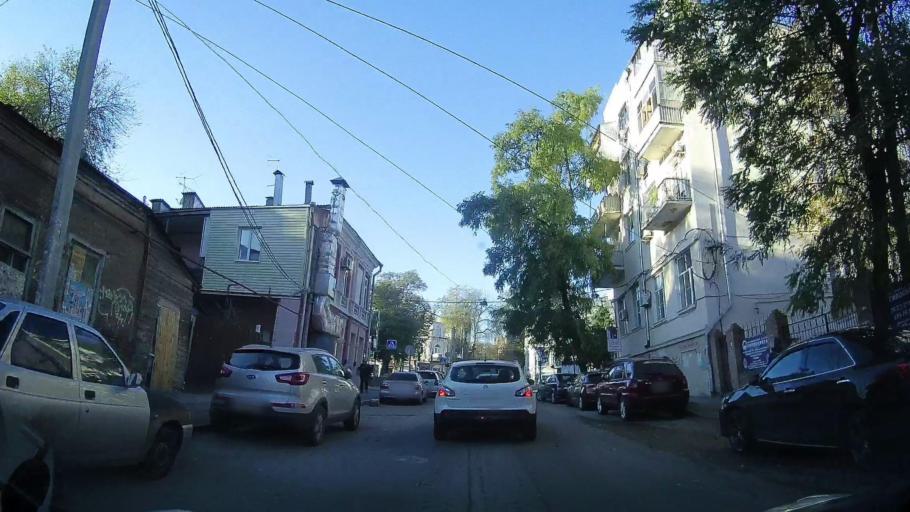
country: RU
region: Rostov
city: Rostov-na-Donu
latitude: 47.2222
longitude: 39.7038
